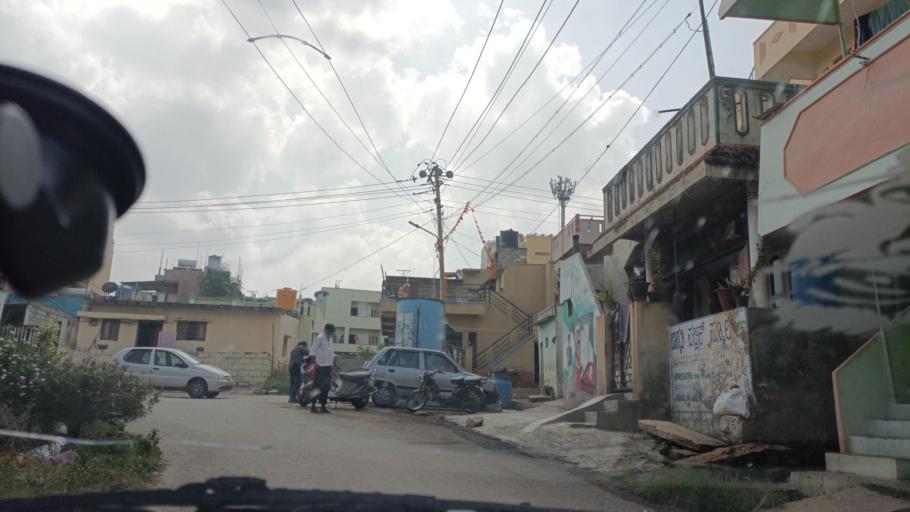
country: IN
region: Karnataka
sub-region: Bangalore Urban
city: Yelahanka
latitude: 13.1670
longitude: 77.6343
